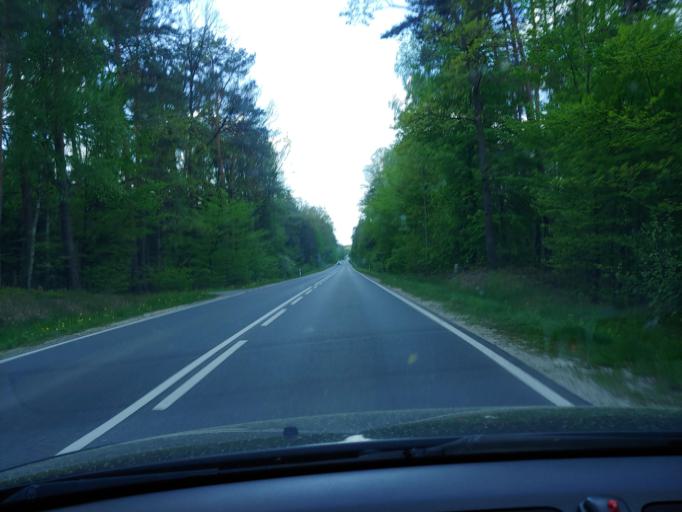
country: PL
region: Lesser Poland Voivodeship
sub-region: Powiat dabrowski
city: Radgoszcz
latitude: 50.1347
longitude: 21.1615
